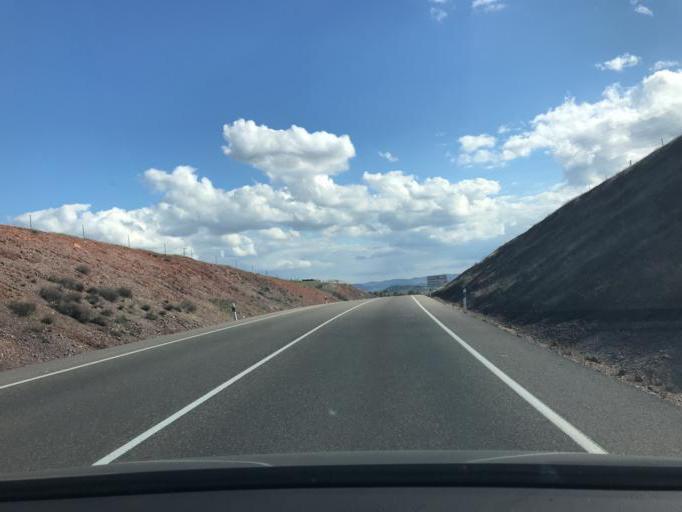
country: ES
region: Andalusia
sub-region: Province of Cordoba
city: Penarroya-Pueblonuevo
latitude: 38.3049
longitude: -5.2575
